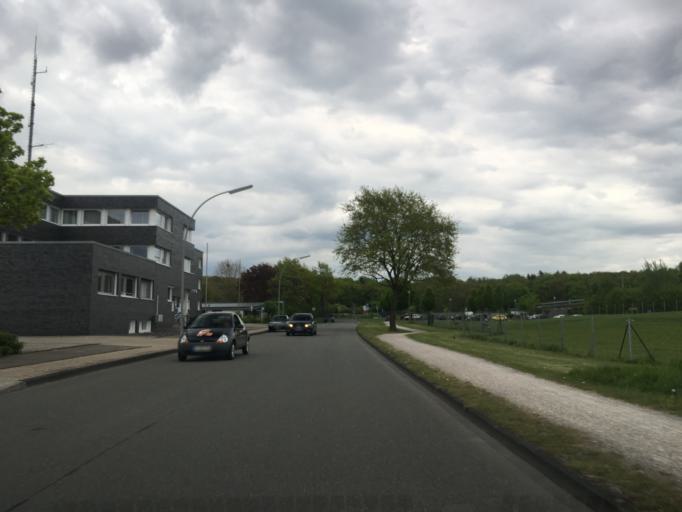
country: DE
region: North Rhine-Westphalia
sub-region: Regierungsbezirk Munster
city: Steinfurt
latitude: 52.1472
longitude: 7.3471
